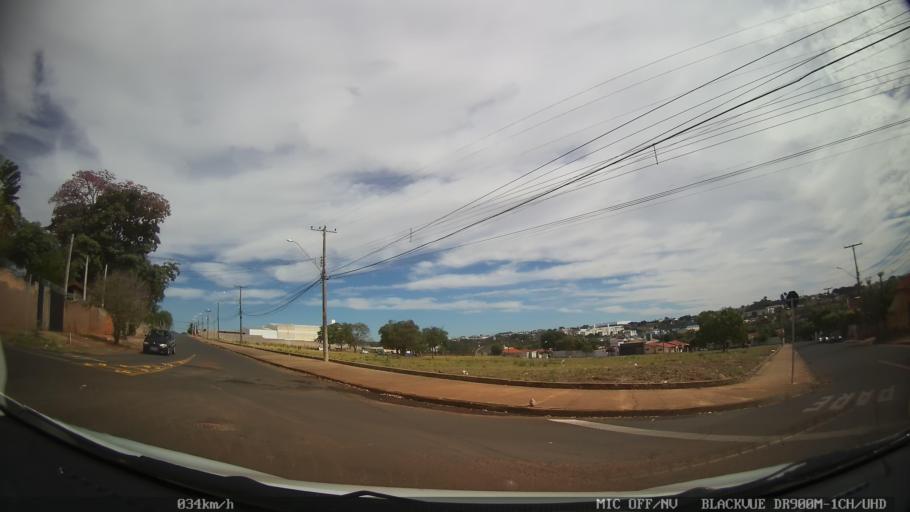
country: BR
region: Sao Paulo
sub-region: Catanduva
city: Catanduva
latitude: -21.1567
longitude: -48.9776
